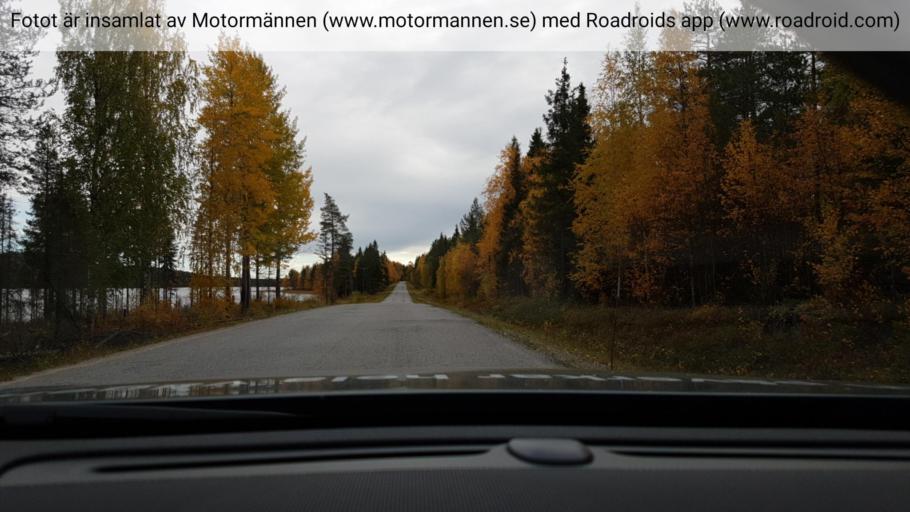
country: SE
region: Norrbotten
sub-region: Overkalix Kommun
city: OEverkalix
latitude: 66.2429
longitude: 23.0032
